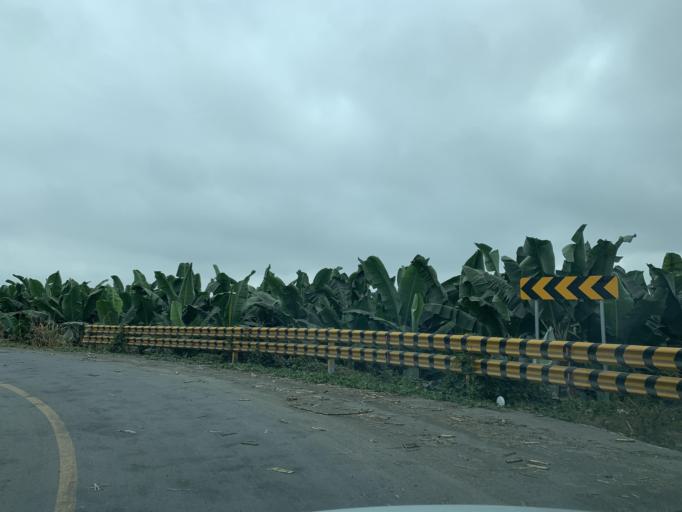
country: EC
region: Guayas
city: Coronel Marcelino Mariduena
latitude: -2.3047
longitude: -79.5010
